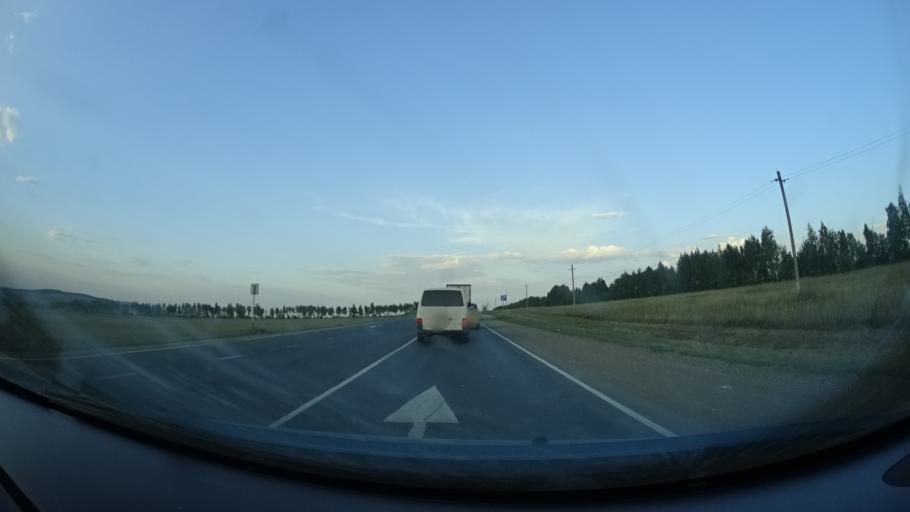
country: RU
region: Samara
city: Kamyshla
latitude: 54.0757
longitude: 52.2683
